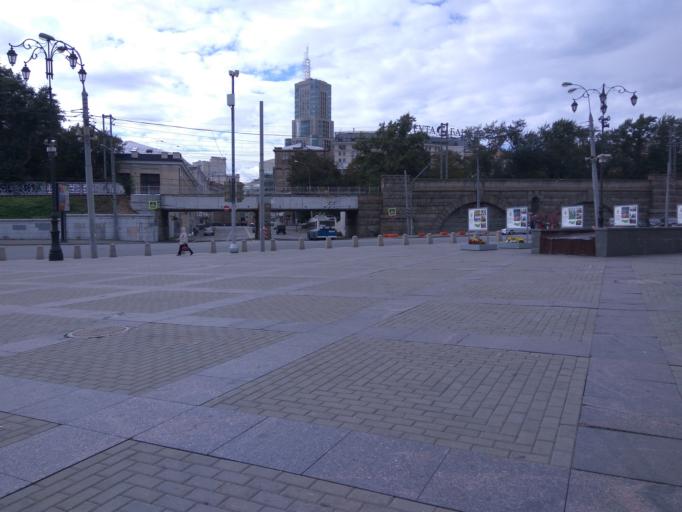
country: RU
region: Moscow
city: Sokol'niki
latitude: 55.7724
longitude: 37.6553
